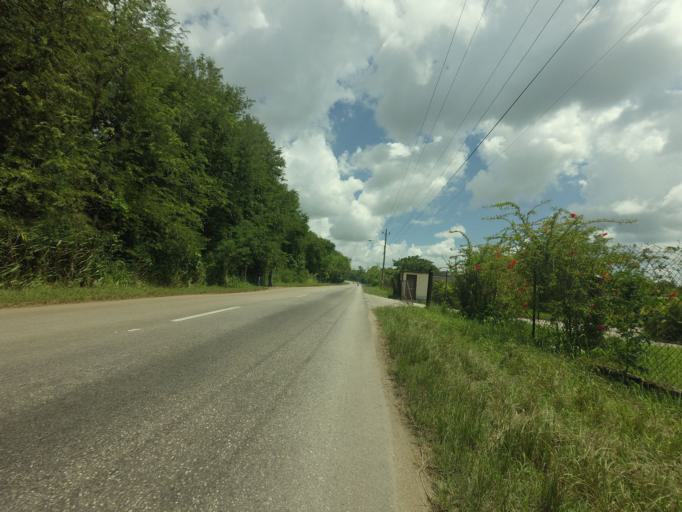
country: CU
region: La Habana
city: Arroyo Naranjo
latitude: 23.0174
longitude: -82.3067
